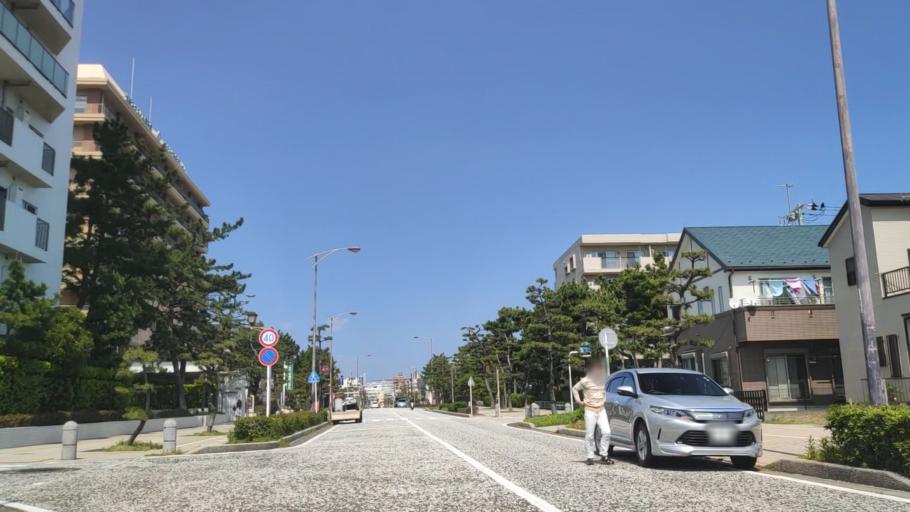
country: JP
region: Kanagawa
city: Hiratsuka
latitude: 35.3187
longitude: 139.3535
